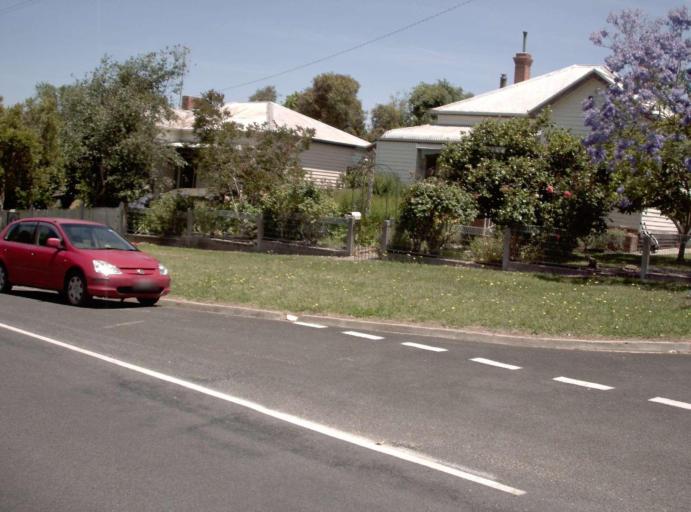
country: AU
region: Victoria
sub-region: East Gippsland
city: Lakes Entrance
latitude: -37.7030
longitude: 147.8337
